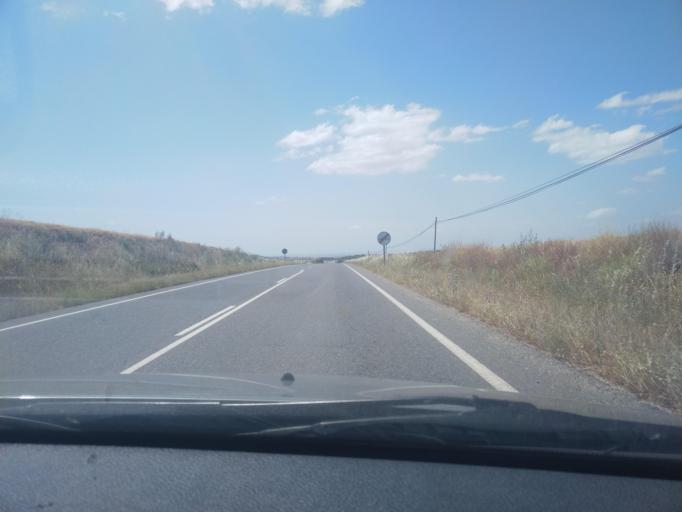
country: ES
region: Castille-La Mancha
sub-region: Province of Toledo
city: Casasbuenas
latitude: 39.7686
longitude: -4.1438
